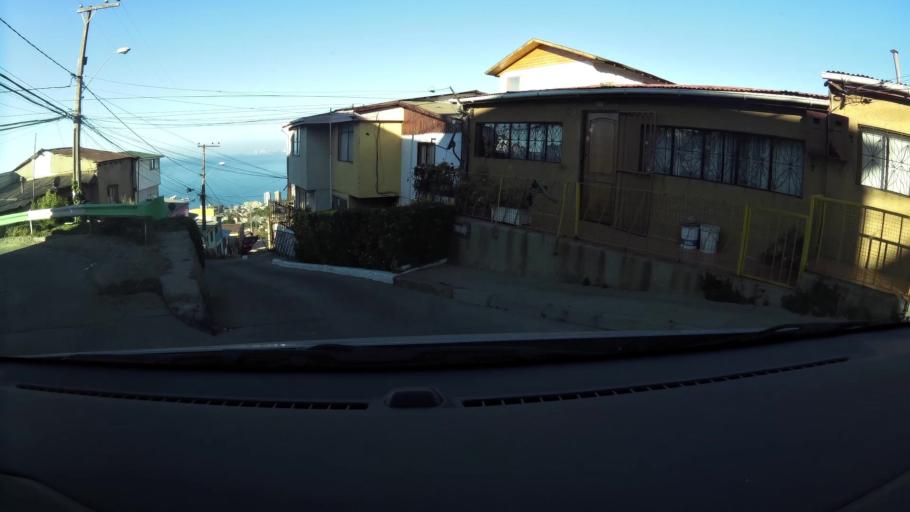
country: CL
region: Valparaiso
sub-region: Provincia de Valparaiso
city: Valparaiso
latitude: -33.0562
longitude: -71.6278
